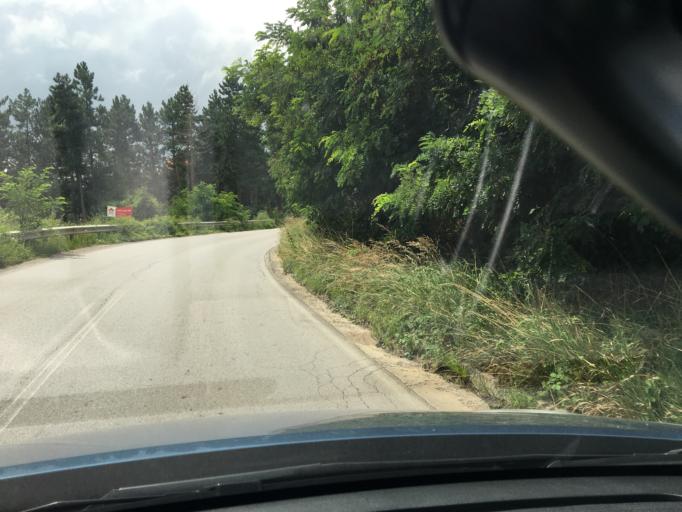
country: BG
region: Sofia-Capital
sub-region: Stolichna Obshtina
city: Sofia
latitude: 42.6014
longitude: 23.3688
